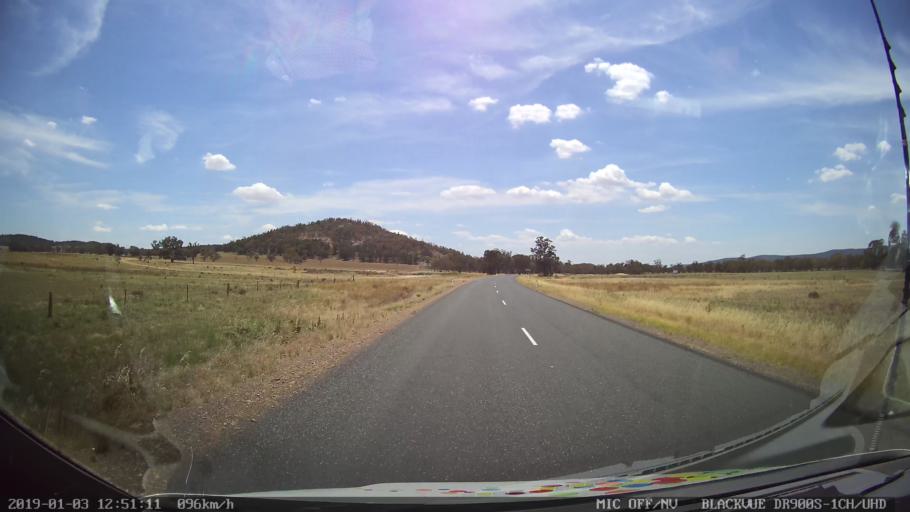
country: AU
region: New South Wales
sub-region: Weddin
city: Grenfell
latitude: -33.6823
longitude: 148.2776
